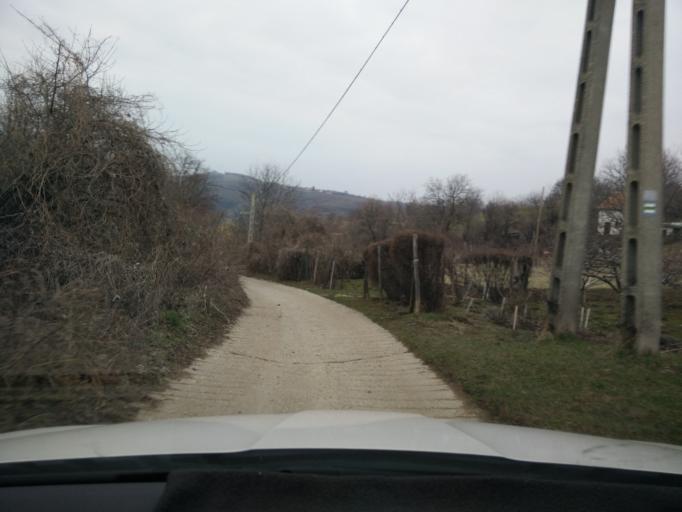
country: HU
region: Tolna
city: Szekszard
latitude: 46.3459
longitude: 18.6758
